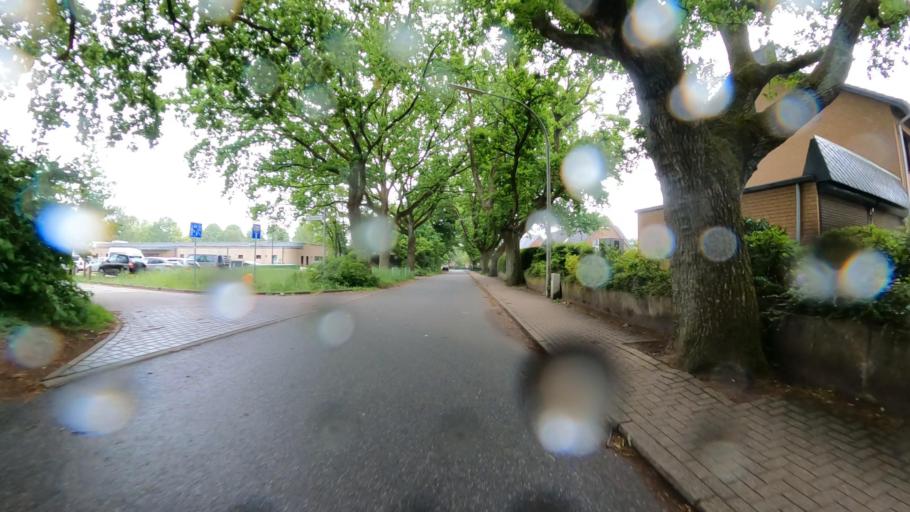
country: DE
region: Hamburg
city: Langenhorn
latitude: 53.6935
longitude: 10.0344
